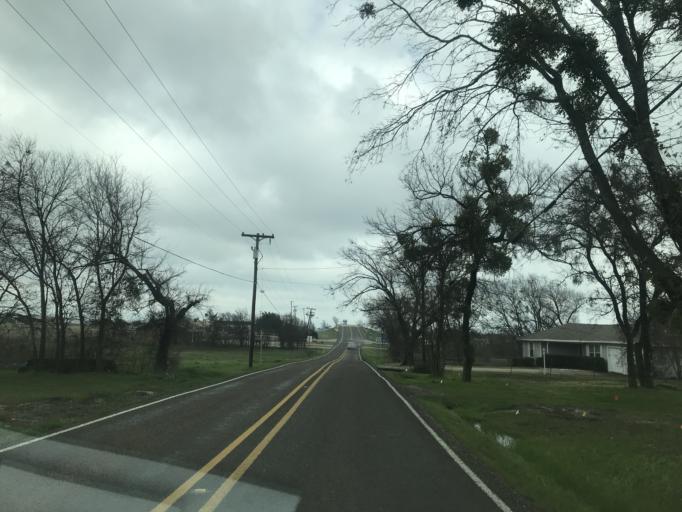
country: US
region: Texas
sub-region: Ellis County
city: Palmer
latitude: 32.4324
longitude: -96.6636
